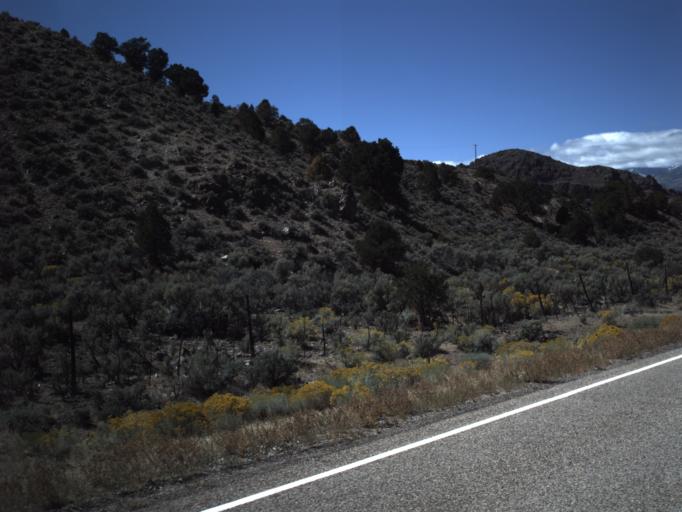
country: US
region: Utah
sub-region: Piute County
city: Junction
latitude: 38.2030
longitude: -112.1586
